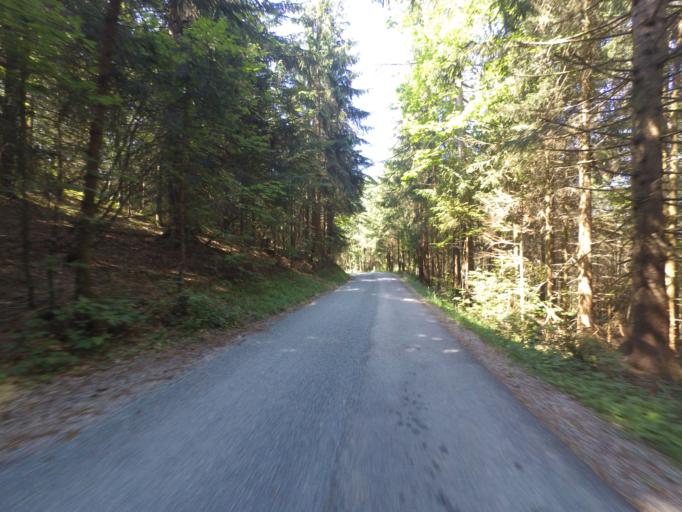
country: AT
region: Salzburg
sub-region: Politischer Bezirk Salzburg-Umgebung
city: Elsbethen
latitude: 47.7547
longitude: 13.1183
